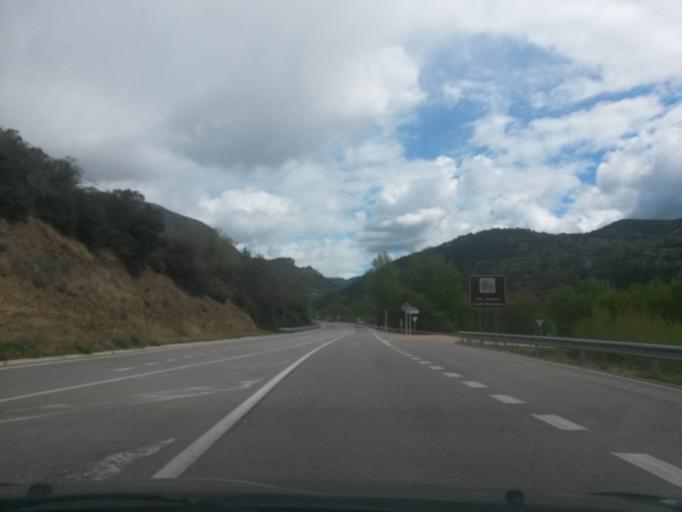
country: ES
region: Catalonia
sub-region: Provincia de Lleida
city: Alas i Cerc
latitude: 42.3574
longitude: 1.5041
